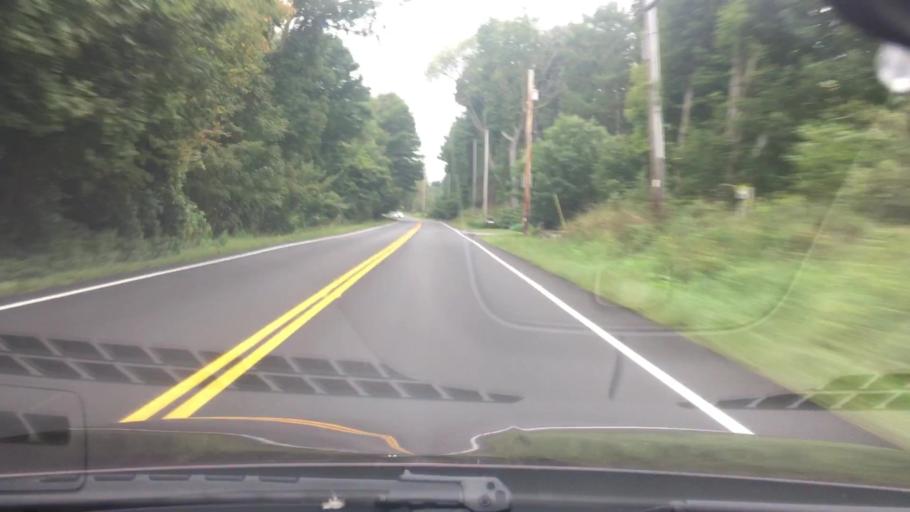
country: US
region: New York
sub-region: Dutchess County
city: Millbrook
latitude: 41.8336
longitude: -73.6152
